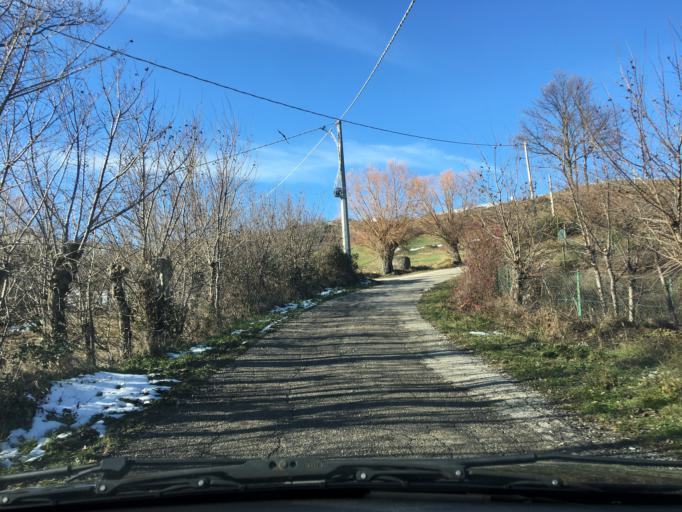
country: IT
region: Molise
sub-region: Provincia di Isernia
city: Agnone
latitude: 41.8459
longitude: 14.3536
